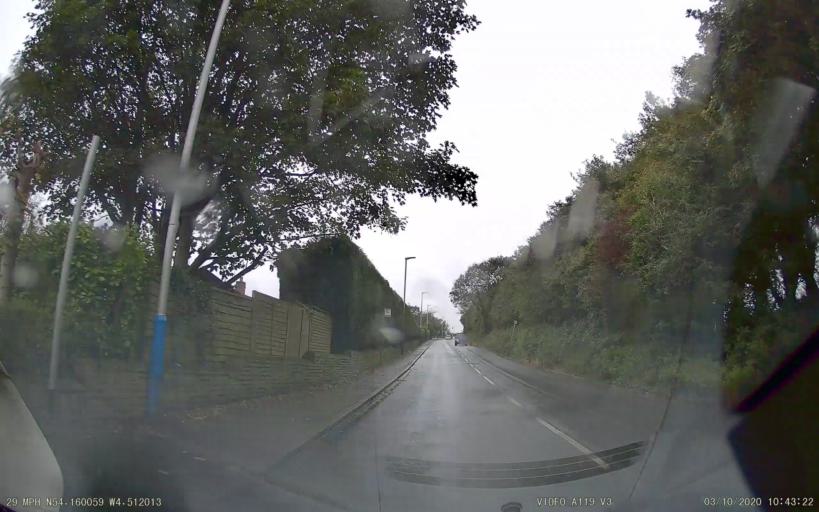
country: IM
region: Douglas
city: Douglas
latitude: 54.1601
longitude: -4.5120
